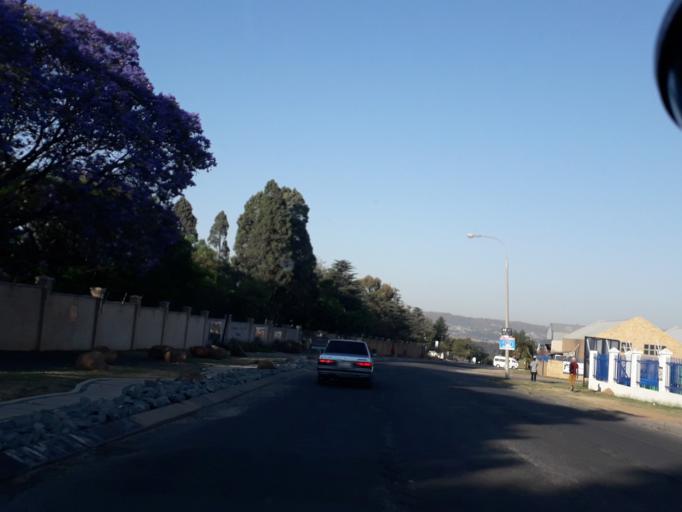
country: ZA
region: Gauteng
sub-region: West Rand District Municipality
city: Muldersdriseloop
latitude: -26.0802
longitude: 27.9191
